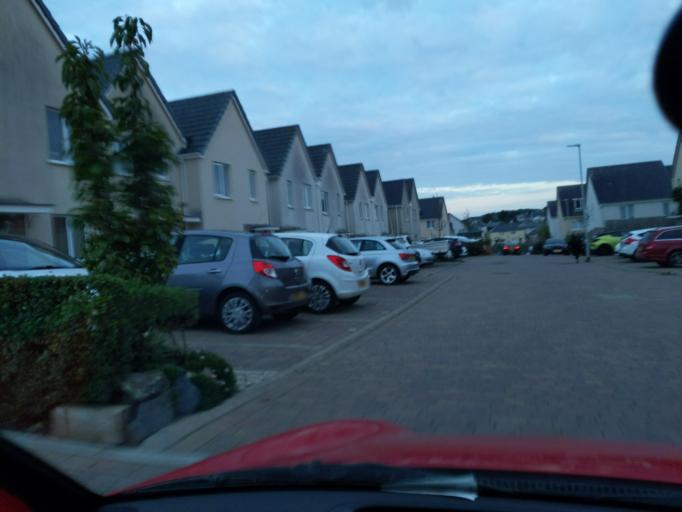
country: GB
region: England
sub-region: Cornwall
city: Millbrook
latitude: 50.3935
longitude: -4.1719
